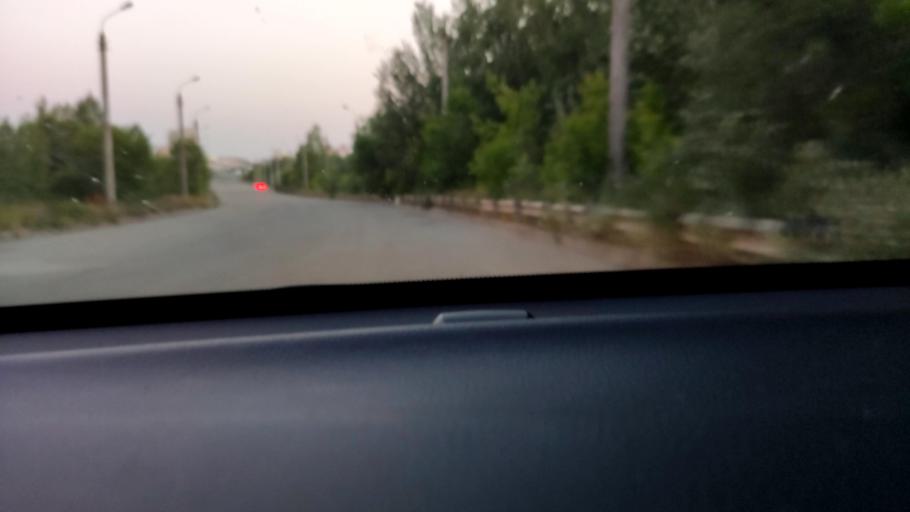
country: RU
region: Tatarstan
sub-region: Gorod Kazan'
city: Kazan
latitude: 55.8236
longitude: 49.1719
